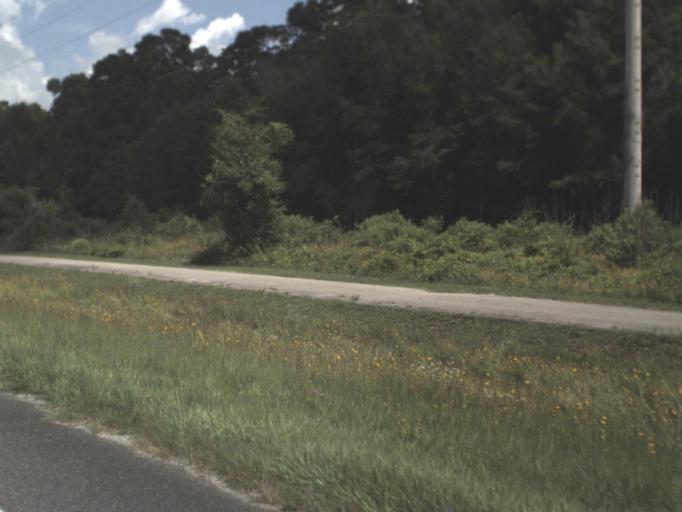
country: US
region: Florida
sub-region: Alachua County
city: High Springs
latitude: 29.9532
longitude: -82.8012
